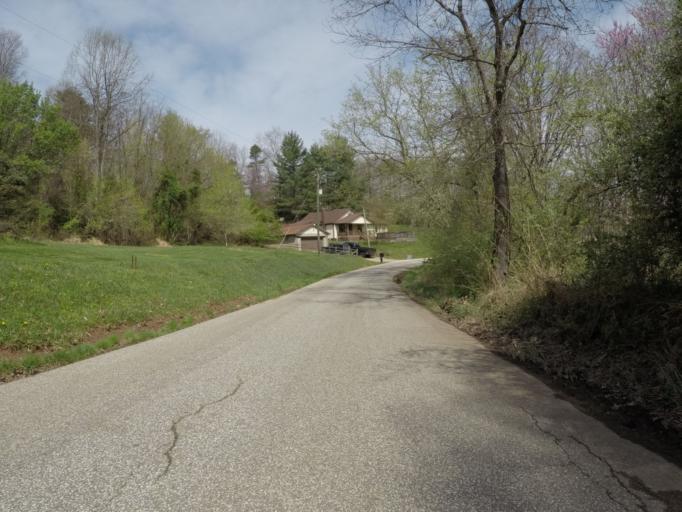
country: US
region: West Virginia
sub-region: Wayne County
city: Lavalette
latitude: 38.3377
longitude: -82.3621
